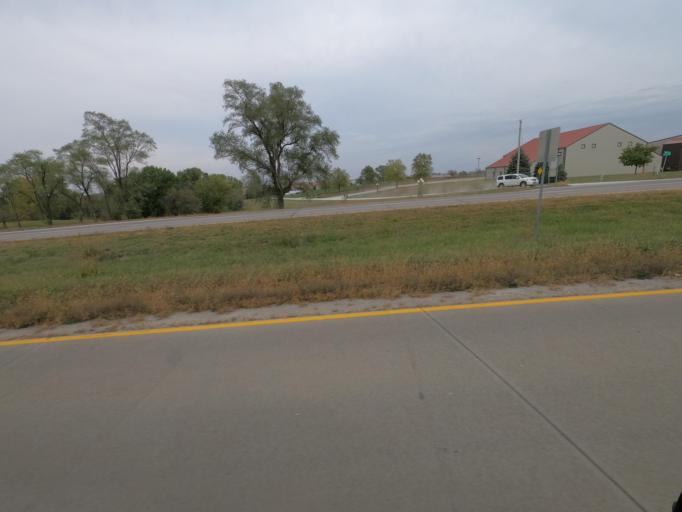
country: US
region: Iowa
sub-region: Marion County
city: Pella
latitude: 41.4249
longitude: -92.9724
